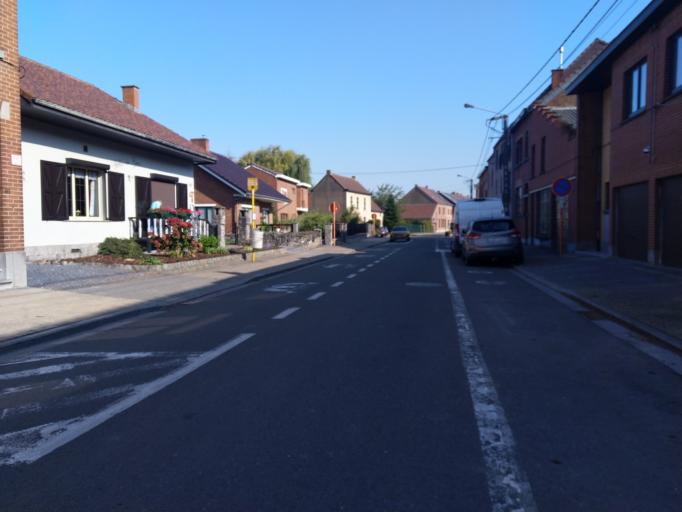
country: BE
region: Wallonia
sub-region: Province du Hainaut
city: Soignies
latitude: 50.5500
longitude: 4.0968
